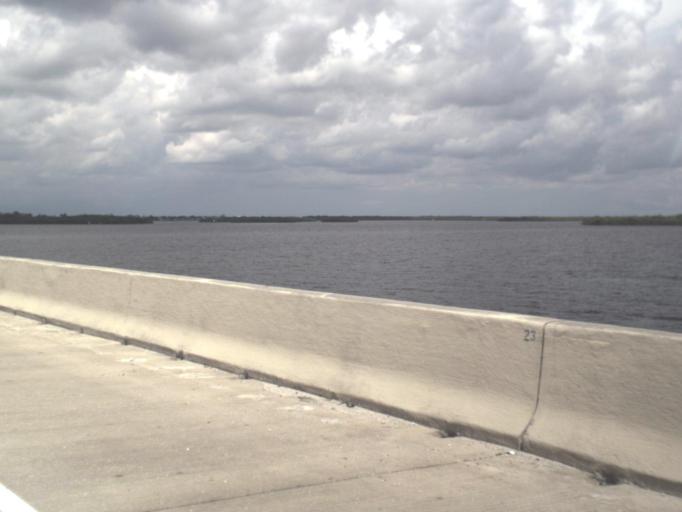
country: US
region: Florida
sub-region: Charlotte County
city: Punta Gorda
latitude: 26.9536
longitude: -82.0205
